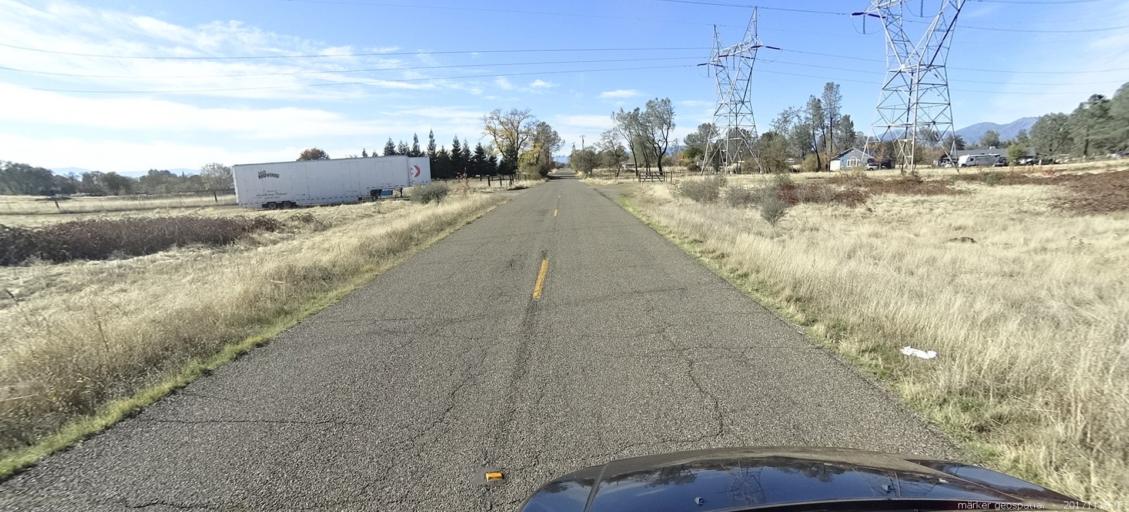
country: US
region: California
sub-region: Shasta County
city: Anderson
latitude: 40.4394
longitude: -122.4148
